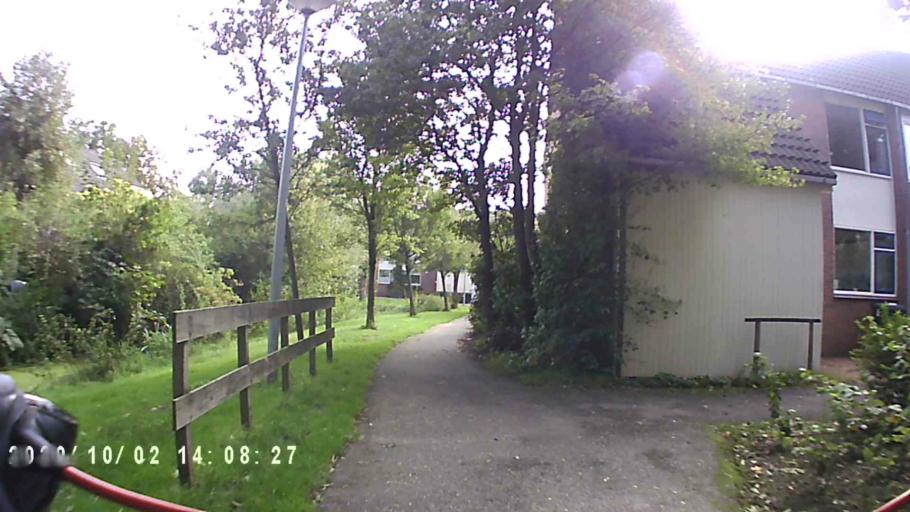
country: NL
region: Groningen
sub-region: Gemeente Zuidhorn
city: Zuidhorn
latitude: 53.2476
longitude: 6.3995
